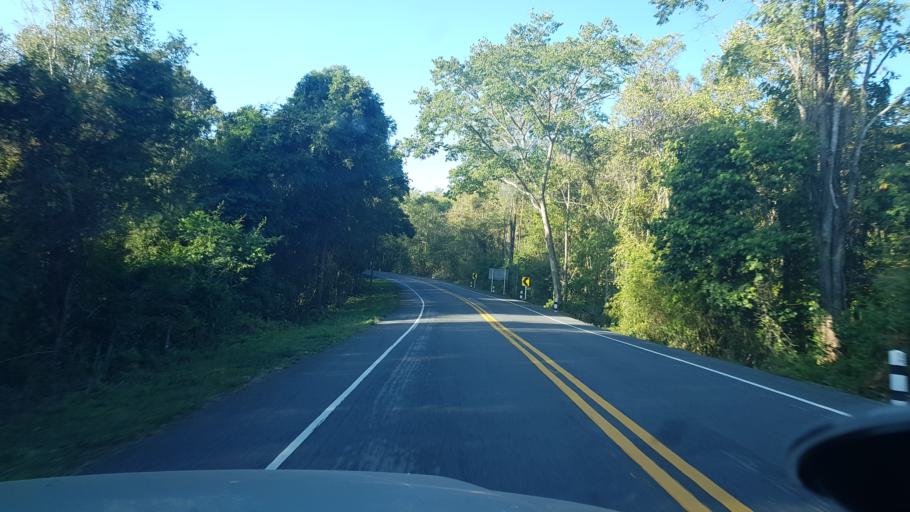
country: TH
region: Phetchabun
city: Nam Nao
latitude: 16.7000
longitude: 101.6422
